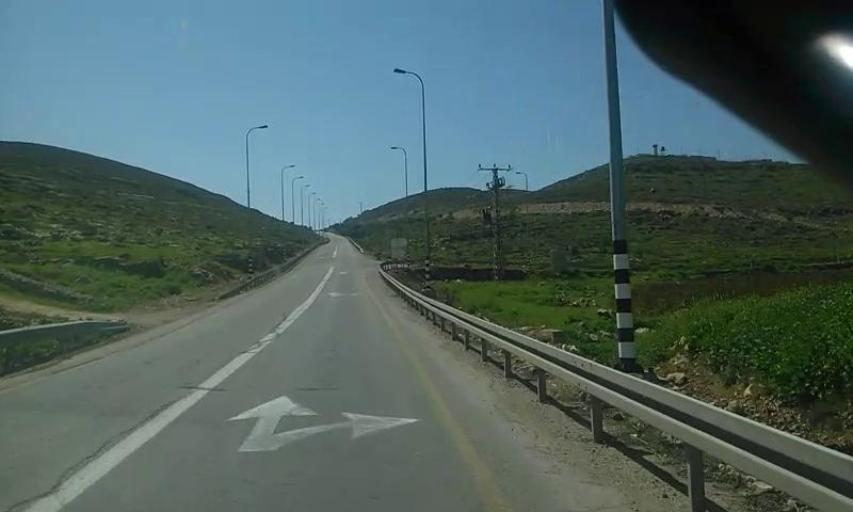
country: PS
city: Khursa
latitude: 31.4806
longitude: 35.0470
